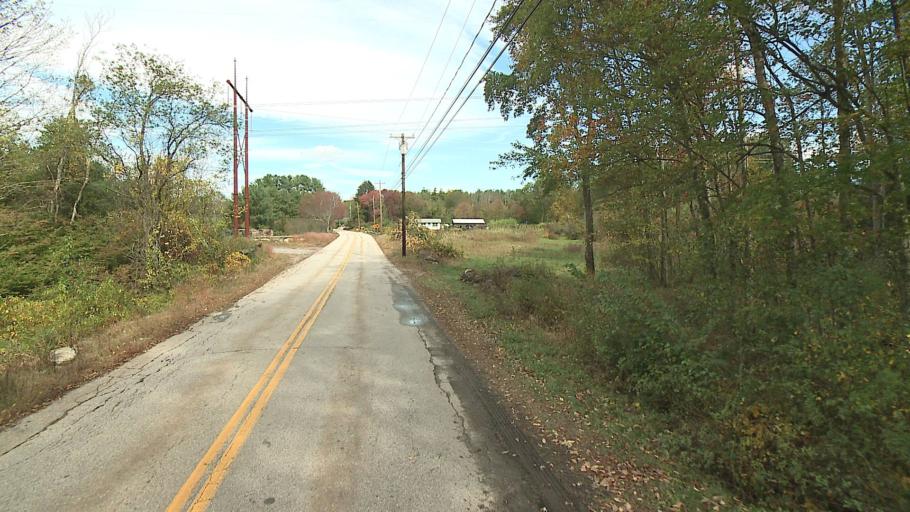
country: US
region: Connecticut
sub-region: Windham County
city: Thompson
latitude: 41.9356
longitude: -71.8216
